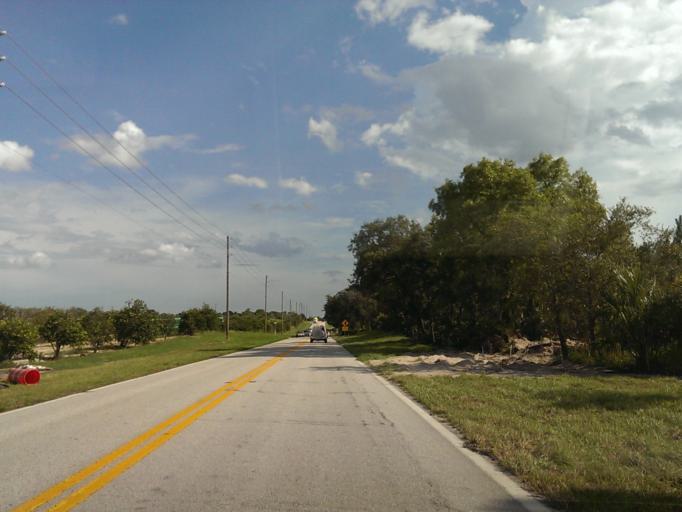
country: US
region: Florida
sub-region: Polk County
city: Citrus Ridge
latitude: 28.4165
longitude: -81.6359
